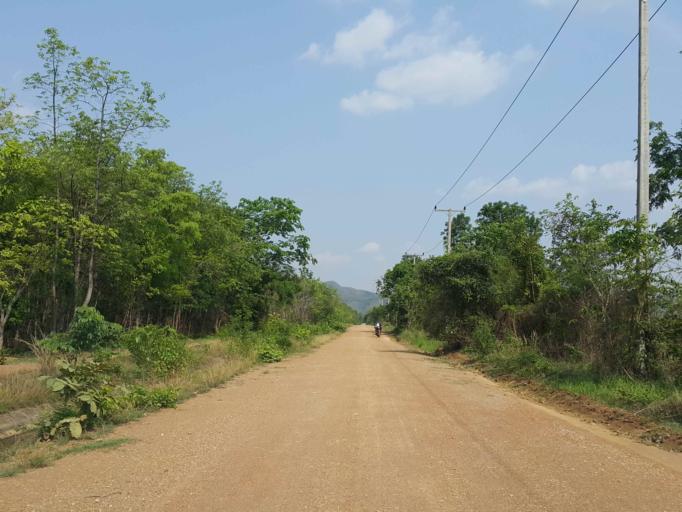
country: TH
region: Sukhothai
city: Thung Saliam
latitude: 17.3339
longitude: 99.4313
